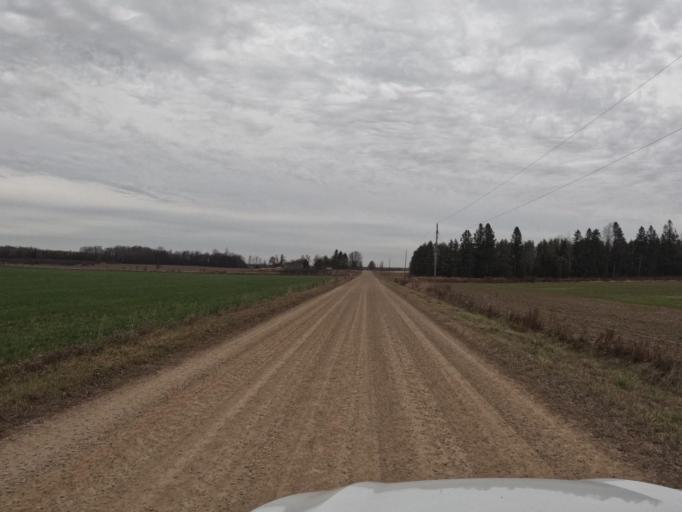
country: CA
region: Ontario
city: Shelburne
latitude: 44.0223
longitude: -80.3695
